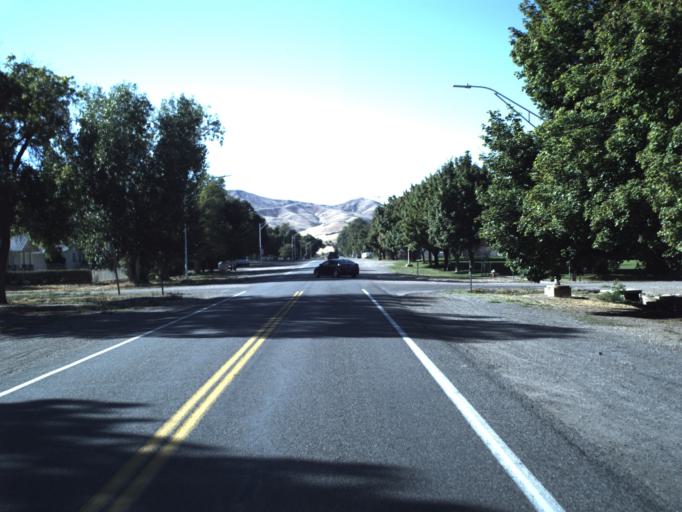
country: US
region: Utah
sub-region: Millard County
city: Delta
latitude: 39.3777
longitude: -112.3361
